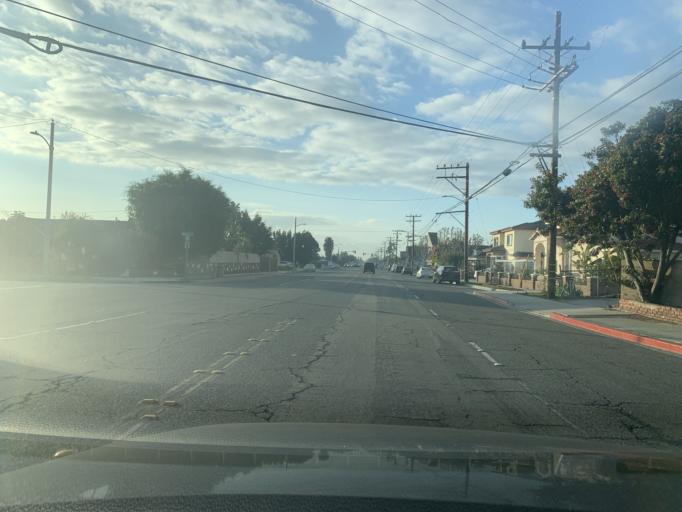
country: US
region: California
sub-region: Orange County
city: Westminster
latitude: 33.7687
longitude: -118.0161
